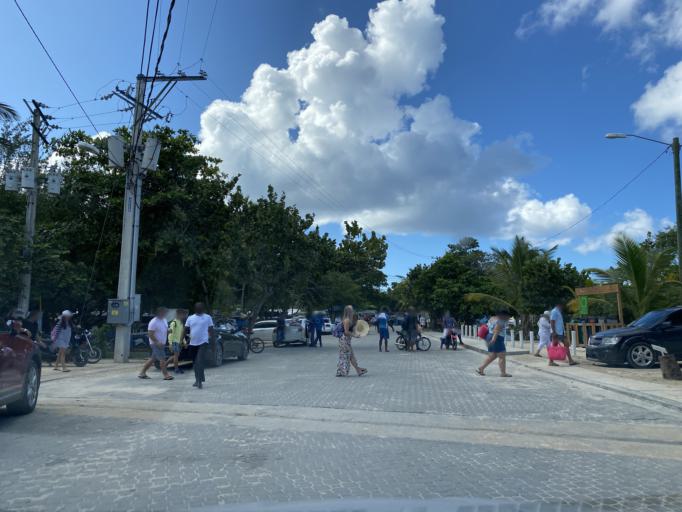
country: DO
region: La Romana
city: La Romana
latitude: 18.3669
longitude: -68.8406
